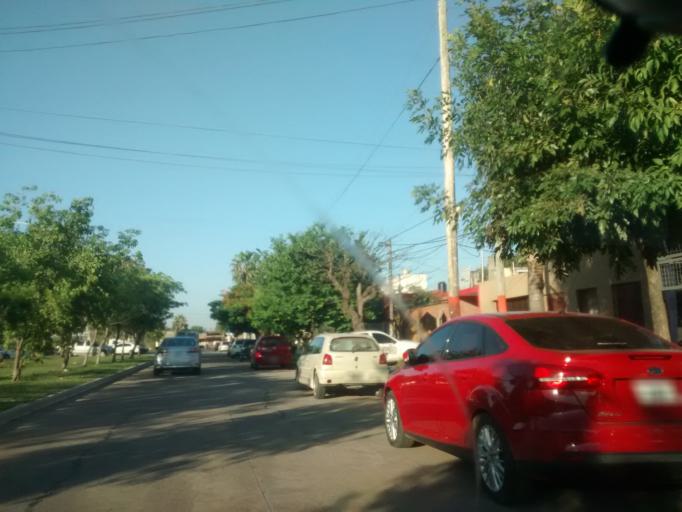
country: AR
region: Chaco
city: Resistencia
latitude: -27.4689
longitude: -58.9924
